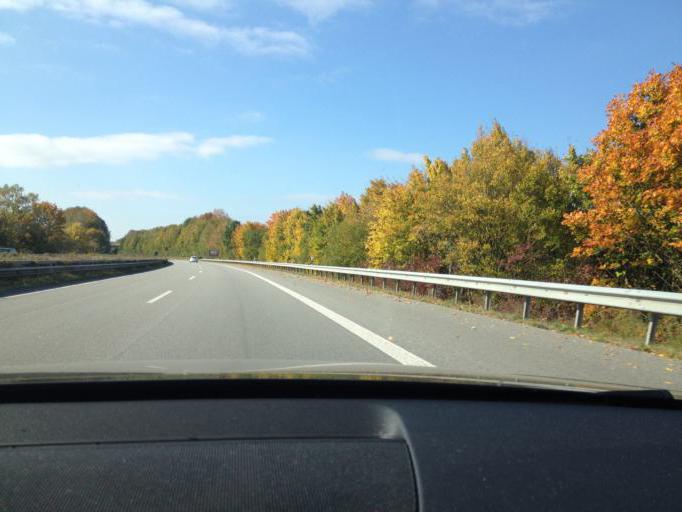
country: DE
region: Rheinland-Pfalz
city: Contwig
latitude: 49.2283
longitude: 7.4322
